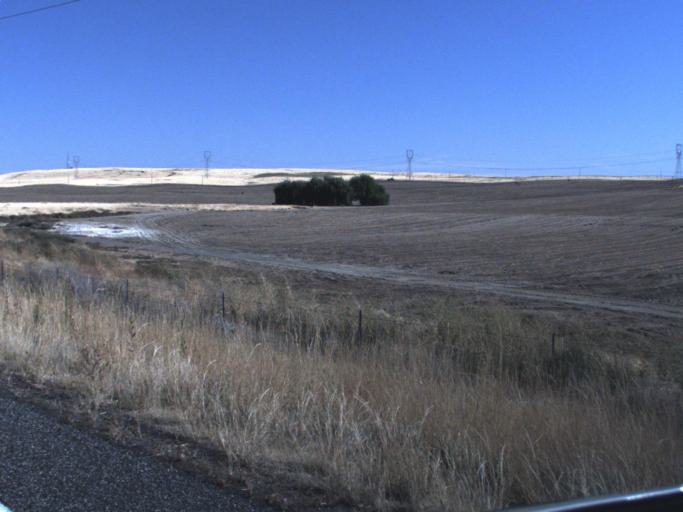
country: US
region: Washington
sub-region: Walla Walla County
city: Burbank
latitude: 46.2890
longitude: -118.7369
